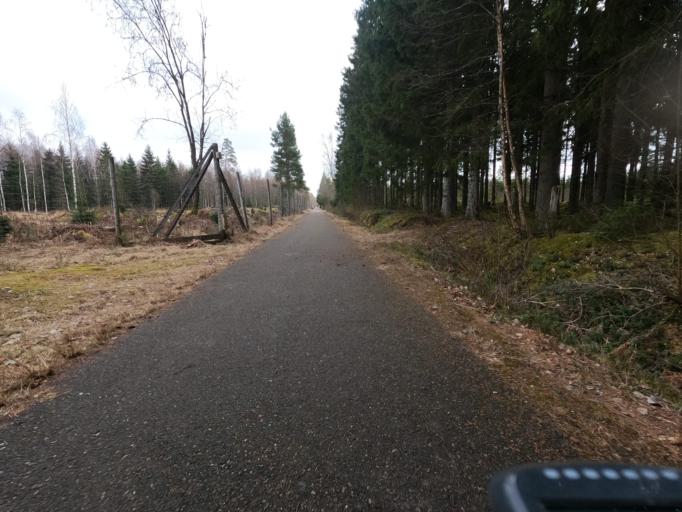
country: SE
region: Joenkoeping
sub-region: Varnamo Kommun
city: Rydaholm
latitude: 56.8580
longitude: 14.1795
